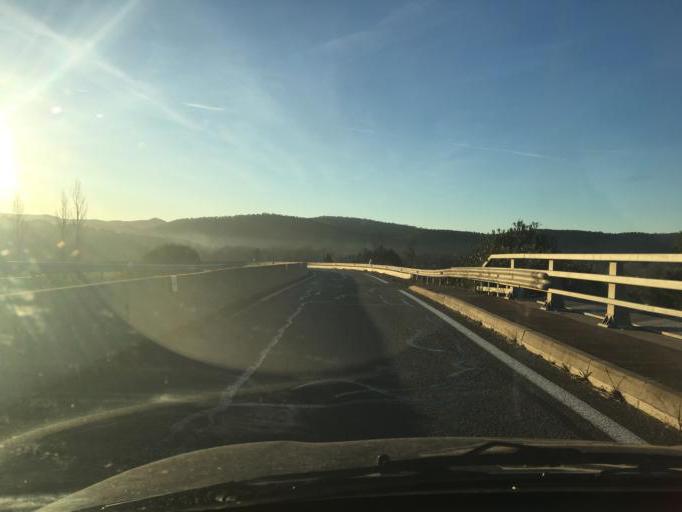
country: FR
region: Provence-Alpes-Cote d'Azur
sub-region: Departement du Var
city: Les Arcs
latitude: 43.4503
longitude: 6.4924
